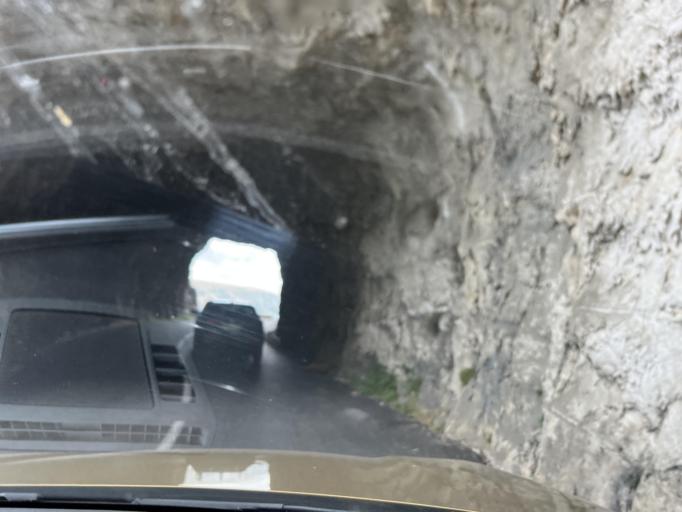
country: FR
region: Provence-Alpes-Cote d'Azur
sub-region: Departement des Alpes-Maritimes
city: Saint-Vallier-de-Thiey
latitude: 43.7966
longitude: 6.9174
